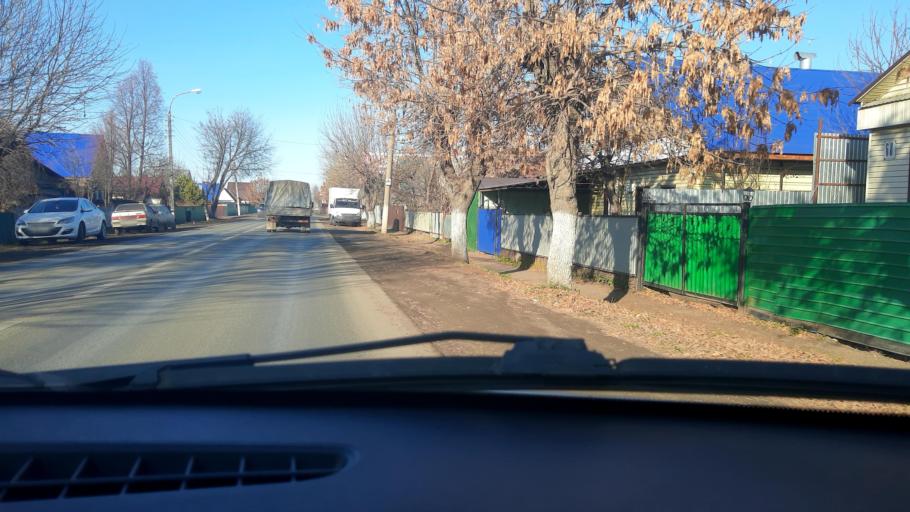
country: RU
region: Bashkortostan
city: Avdon
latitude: 54.7048
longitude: 55.8209
